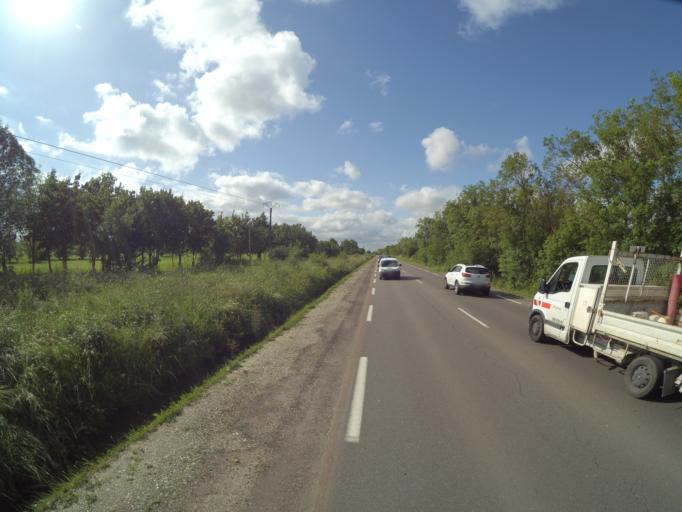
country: FR
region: Aquitaine
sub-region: Departement de la Gironde
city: Bassens
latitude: 44.9091
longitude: -0.5571
